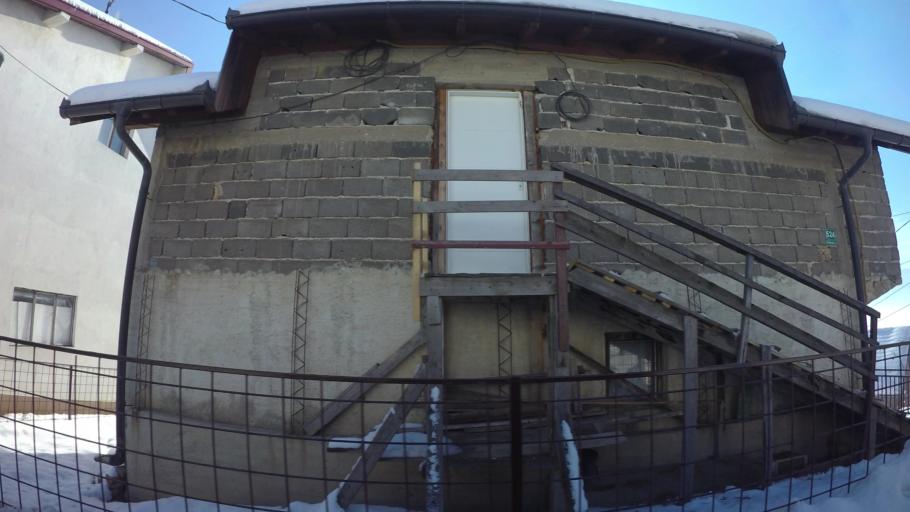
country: BA
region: Federation of Bosnia and Herzegovina
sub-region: Kanton Sarajevo
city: Sarajevo
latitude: 43.8389
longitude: 18.3680
